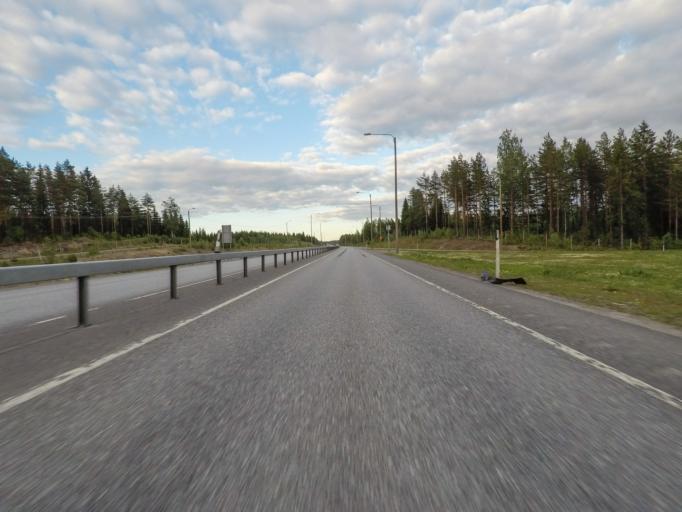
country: FI
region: Southern Savonia
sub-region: Mikkeli
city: Pertunmaa
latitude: 61.4349
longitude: 26.5640
